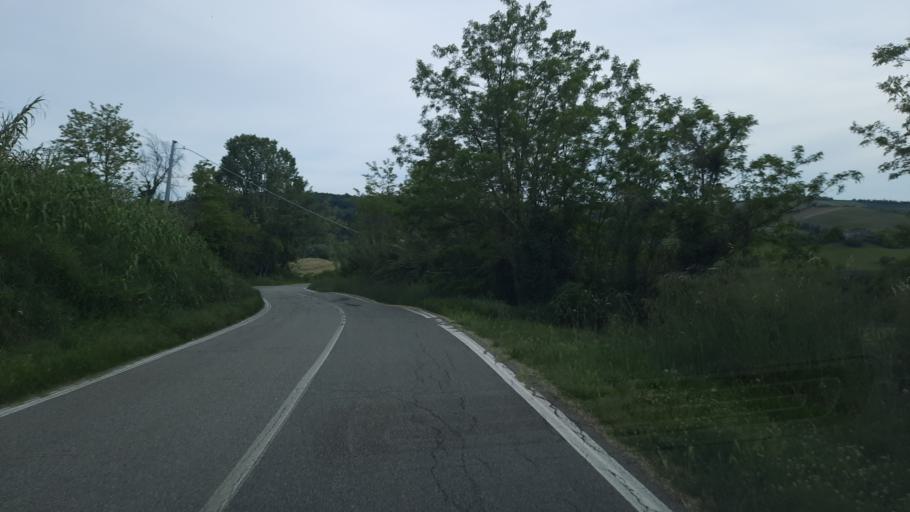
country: IT
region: Piedmont
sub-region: Provincia di Alessandria
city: Coniolo Bricco
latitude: 45.1460
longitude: 8.3800
